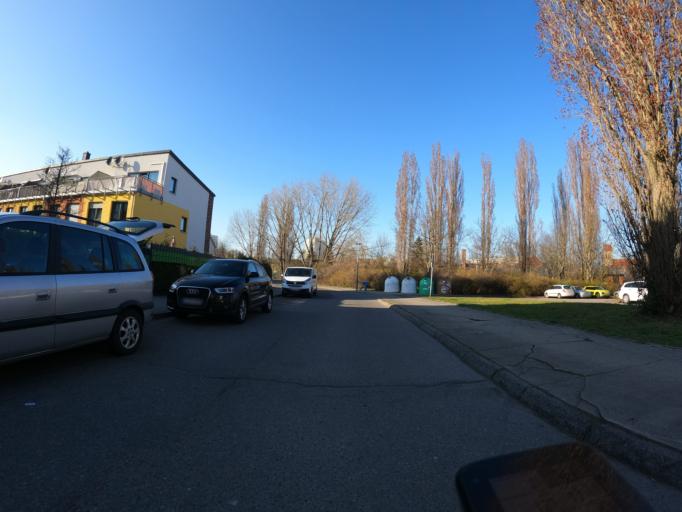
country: DE
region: Berlin
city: Marzahn
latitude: 52.5418
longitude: 13.5596
